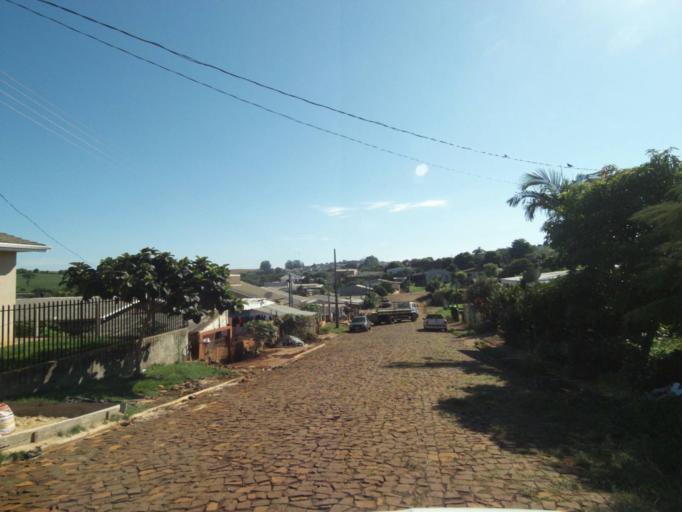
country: BR
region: Parana
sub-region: Laranjeiras Do Sul
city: Laranjeiras do Sul
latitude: -25.4939
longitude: -52.5364
